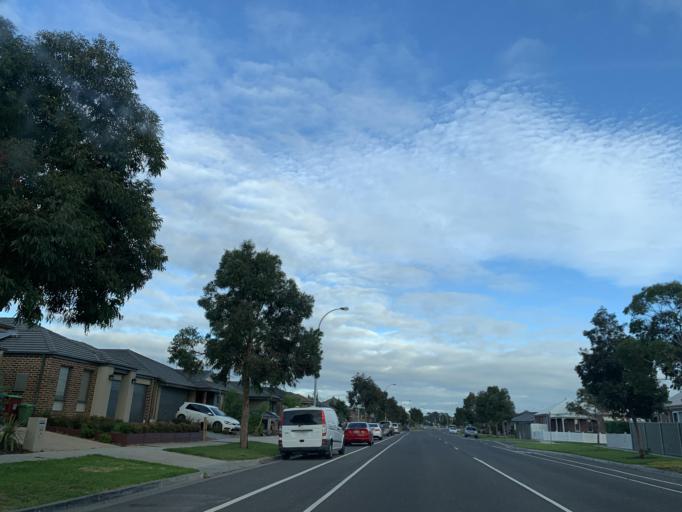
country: AU
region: Victoria
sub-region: Casey
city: Cranbourne East
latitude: -38.1250
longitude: 145.3062
